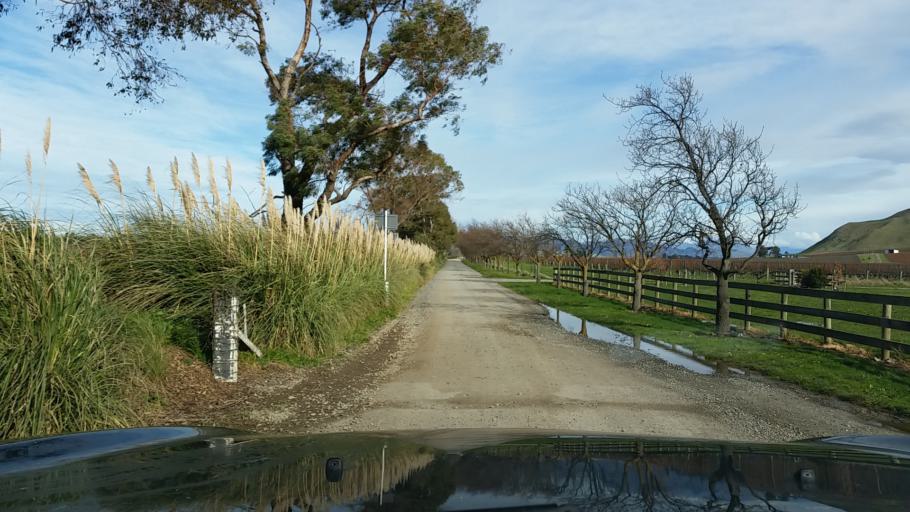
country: NZ
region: Marlborough
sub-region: Marlborough District
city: Blenheim
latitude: -41.6180
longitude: 174.1004
